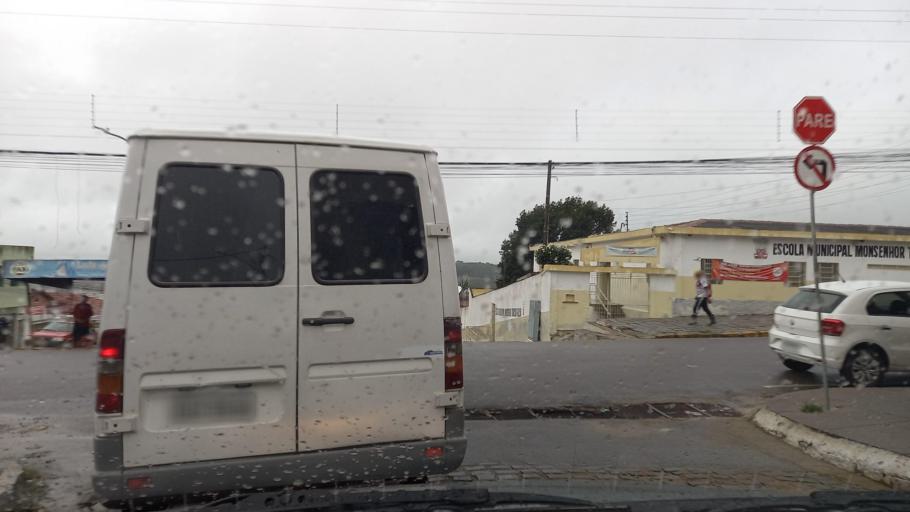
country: BR
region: Pernambuco
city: Garanhuns
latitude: -8.8852
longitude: -36.5014
